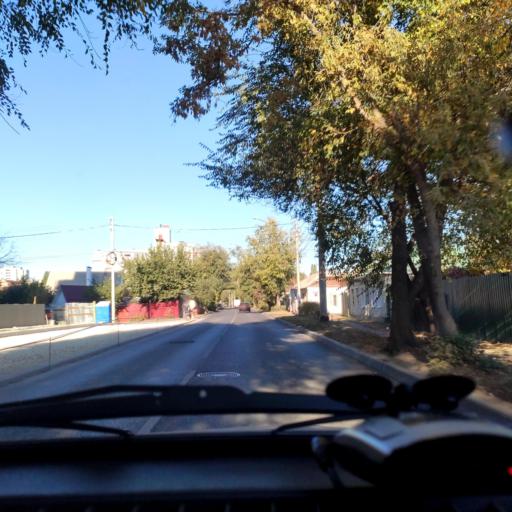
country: RU
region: Voronezj
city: Voronezh
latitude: 51.6440
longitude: 39.1774
